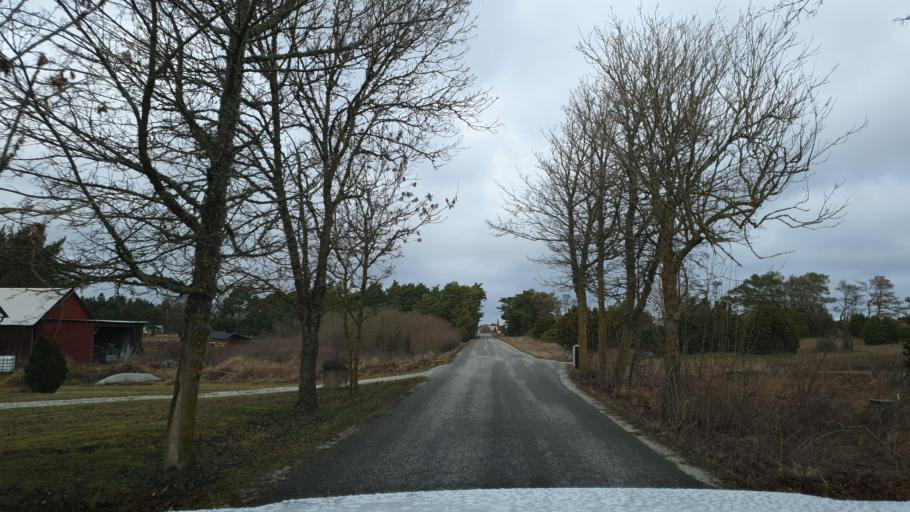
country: SE
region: Gotland
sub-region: Gotland
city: Slite
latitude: 57.3913
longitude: 18.8089
